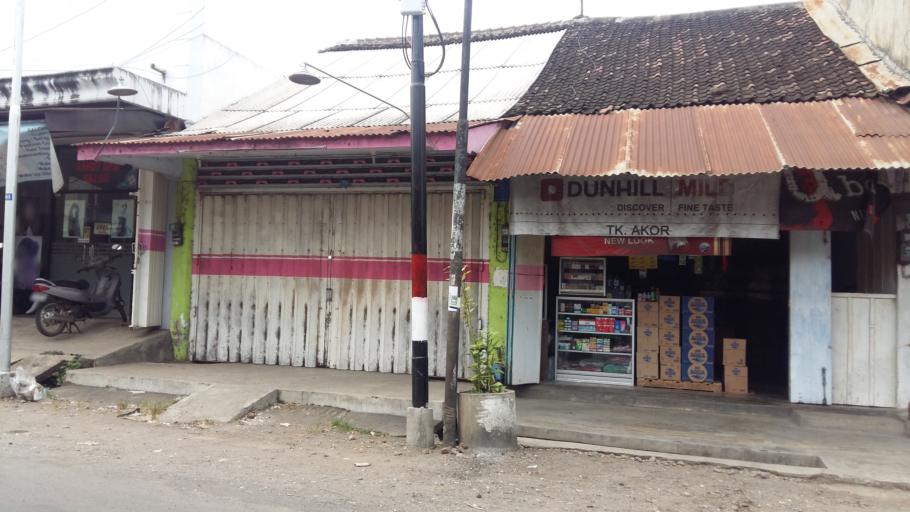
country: ID
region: East Java
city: Krajan
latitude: -8.3067
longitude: 114.2945
